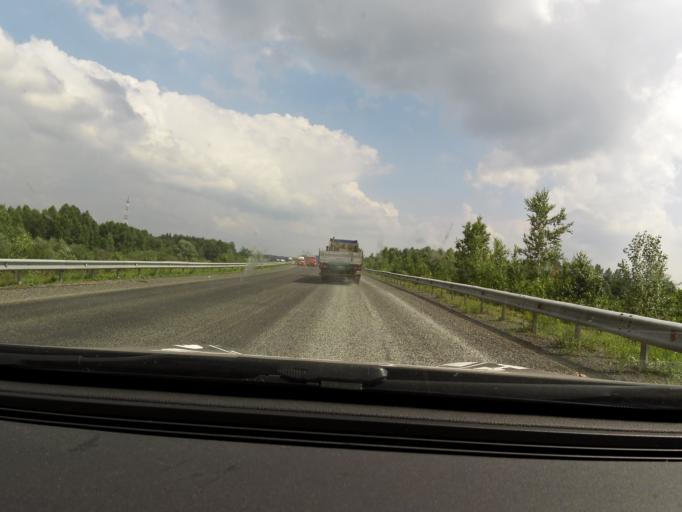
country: RU
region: Sverdlovsk
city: Ufimskiy
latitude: 56.7647
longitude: 58.1388
